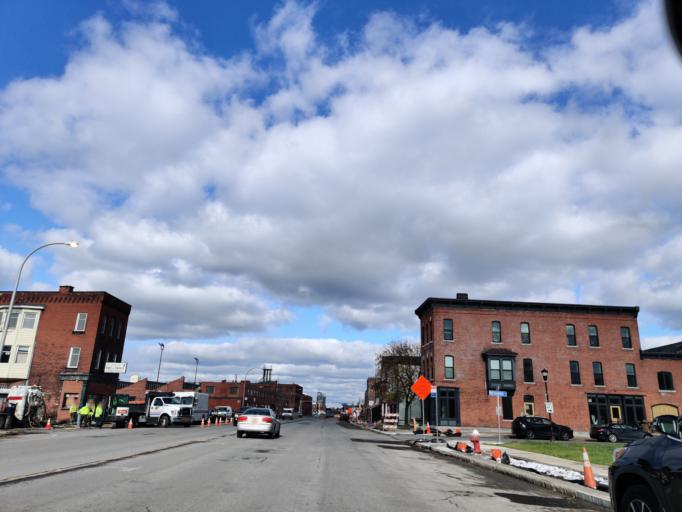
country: US
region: New York
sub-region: Erie County
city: Buffalo
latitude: 42.9167
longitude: -78.8993
